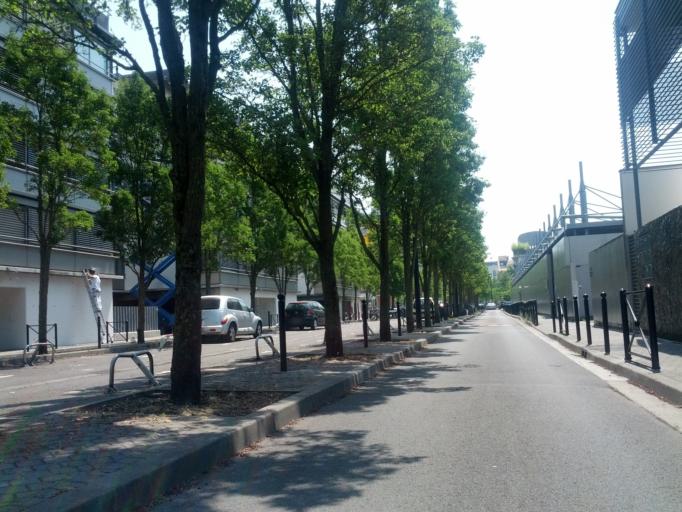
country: FR
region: Aquitaine
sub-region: Departement de la Gironde
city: Bordeaux
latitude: 44.8565
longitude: -0.5683
